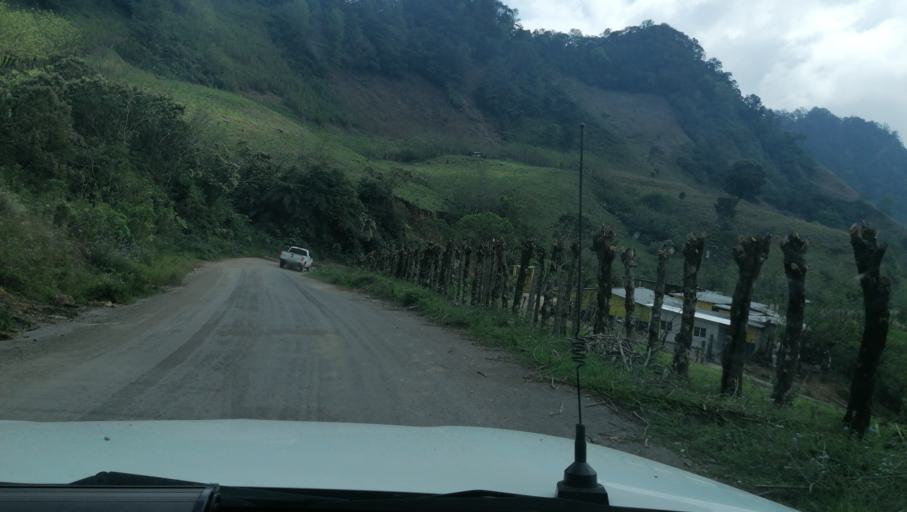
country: MX
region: Chiapas
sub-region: Francisco Leon
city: San Miguel la Sardina
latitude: 17.2501
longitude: -93.2824
